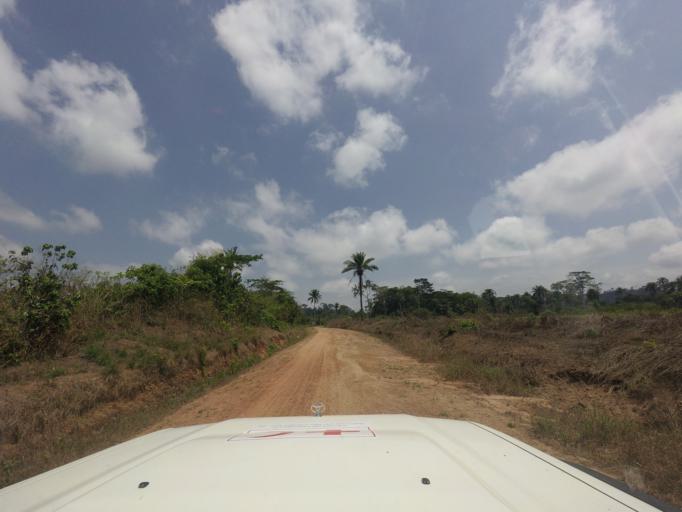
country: LR
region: Lofa
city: Voinjama
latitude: 8.4672
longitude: -9.6648
